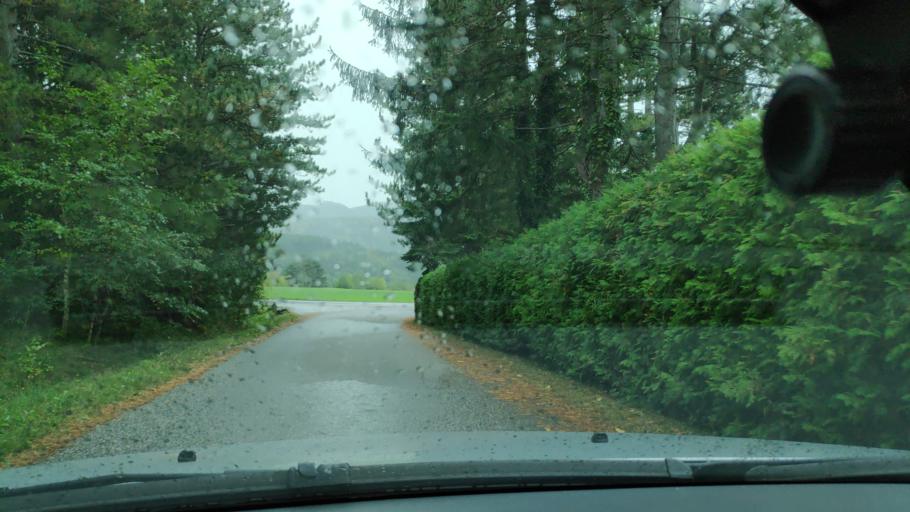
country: AT
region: Lower Austria
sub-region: Politischer Bezirk Neunkirchen
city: Grunbach am Schneeberg
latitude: 47.8006
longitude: 15.9926
